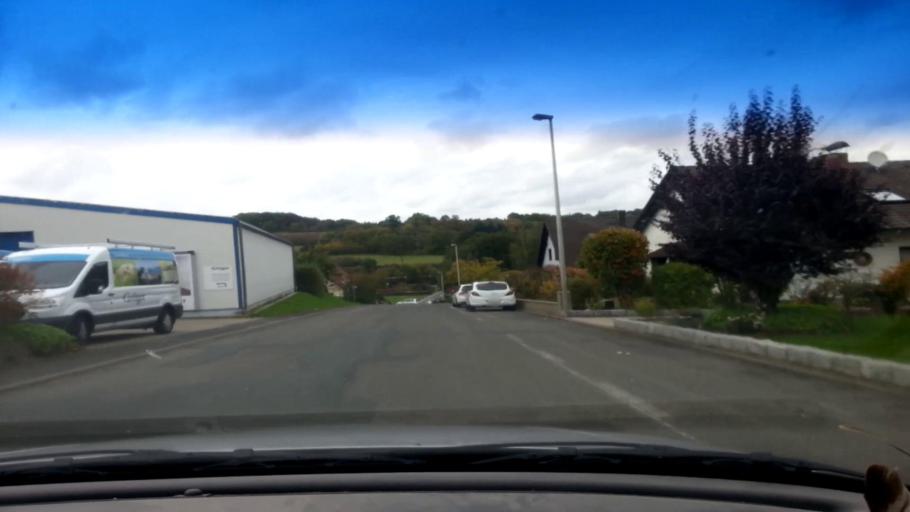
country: DE
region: Bavaria
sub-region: Upper Franconia
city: Gerach
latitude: 50.0311
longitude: 10.8109
